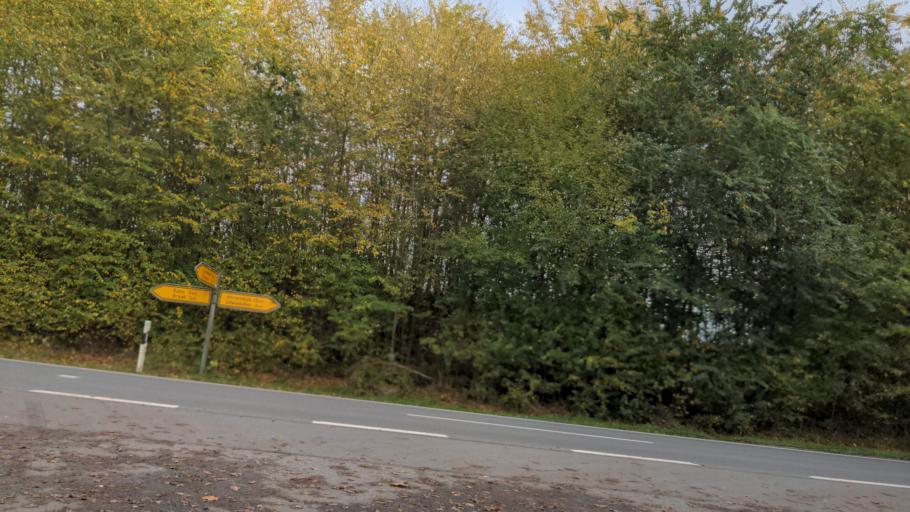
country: DE
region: Schleswig-Holstein
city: Eutin
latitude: 54.0927
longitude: 10.5785
